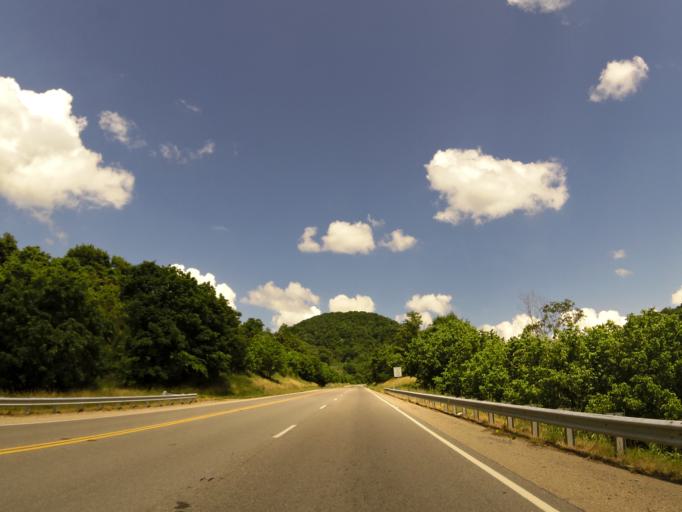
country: US
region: Virginia
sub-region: Lee County
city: Dryden
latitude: 36.7221
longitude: -82.9400
